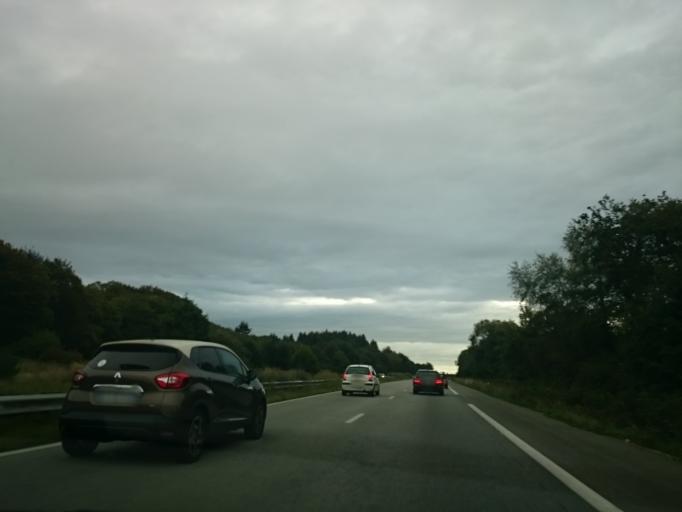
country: FR
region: Brittany
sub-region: Departement du Finistere
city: Saint-Yvi
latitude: 47.9673
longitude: -3.9811
